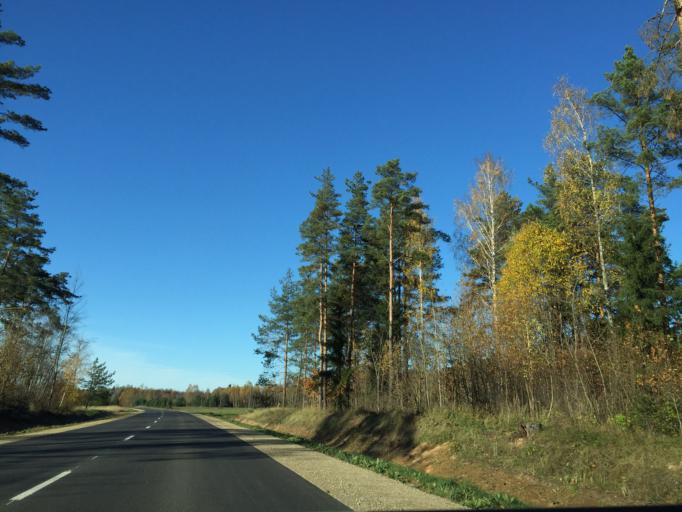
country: LV
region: Aizkraukles Rajons
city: Aizkraukle
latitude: 56.5891
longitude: 25.1896
